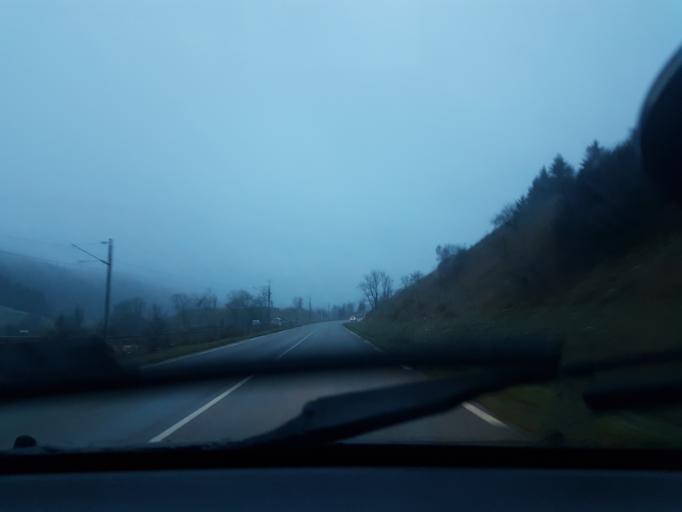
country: FR
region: Franche-Comte
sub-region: Departement du Doubs
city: La Cluse-et-Mijoux
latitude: 46.8738
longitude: 6.3965
